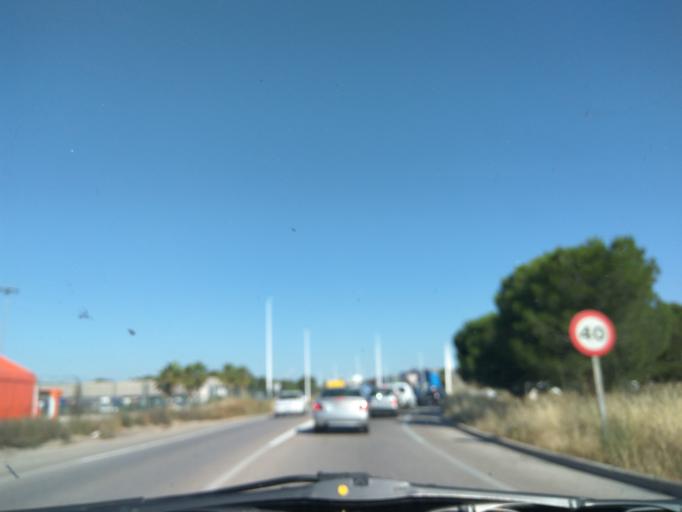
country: ES
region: Valencia
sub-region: Provincia de Valencia
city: Manises
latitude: 39.4961
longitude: -0.4790
